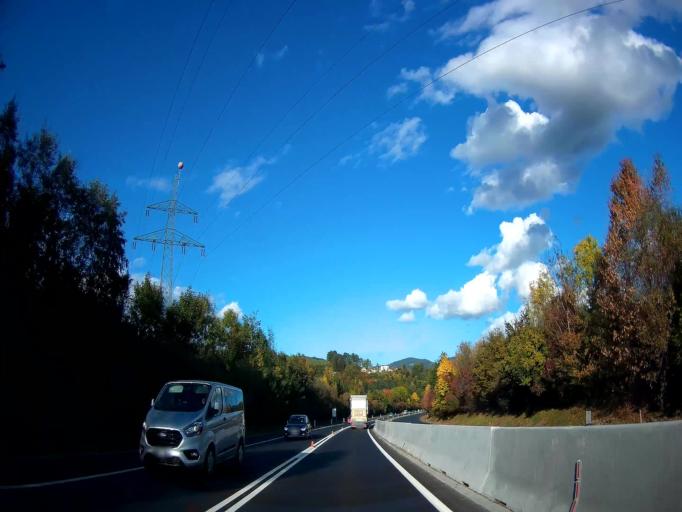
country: AT
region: Carinthia
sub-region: Politischer Bezirk Wolfsberg
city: Wolfsberg
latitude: 46.8409
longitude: 14.8241
